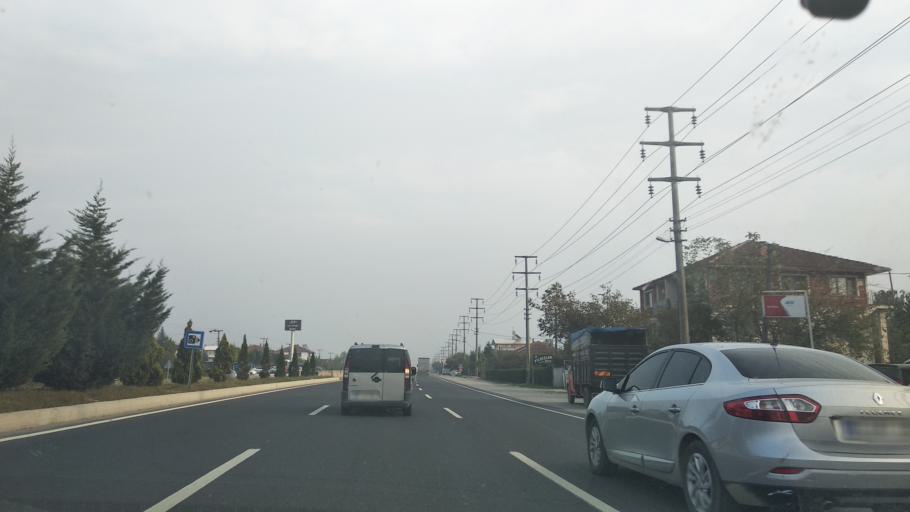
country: TR
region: Duzce
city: Duzce
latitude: 40.8026
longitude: 31.2377
